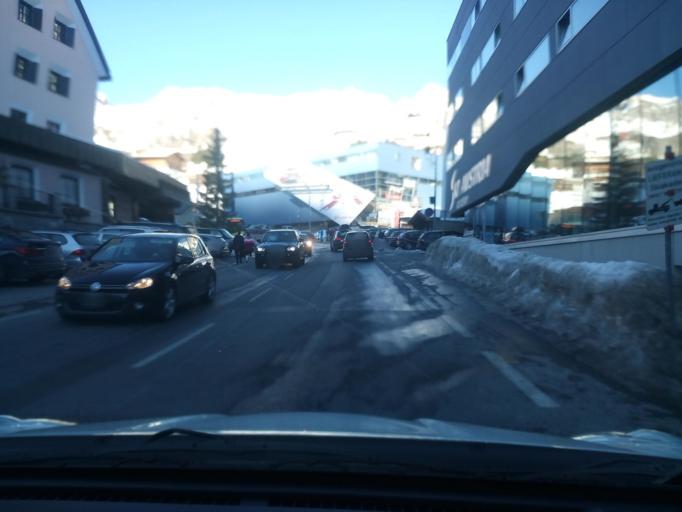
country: AT
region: Tyrol
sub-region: Politischer Bezirk Landeck
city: Sankt Anton am Arlberg
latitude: 47.1259
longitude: 10.2144
